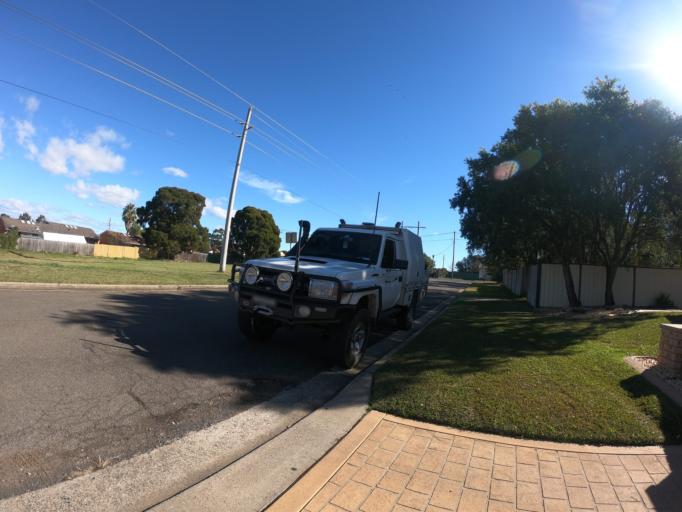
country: AU
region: New South Wales
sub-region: Hawkesbury
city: South Windsor
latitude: -33.6269
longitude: 150.8013
